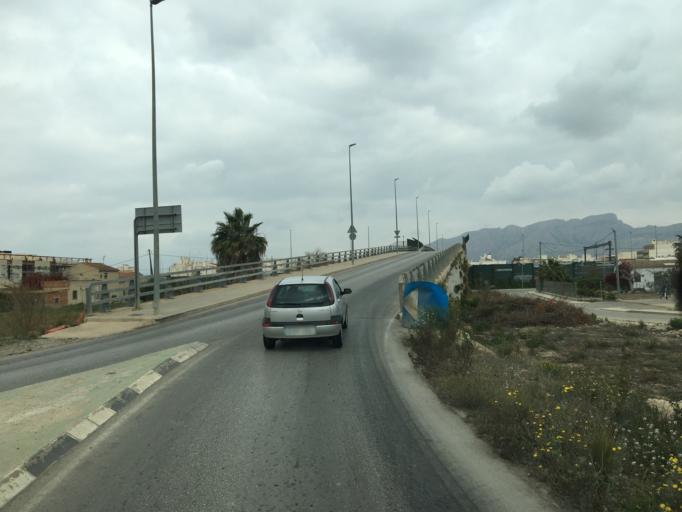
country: ES
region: Murcia
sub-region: Murcia
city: Beniel
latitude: 38.0451
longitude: -0.9961
